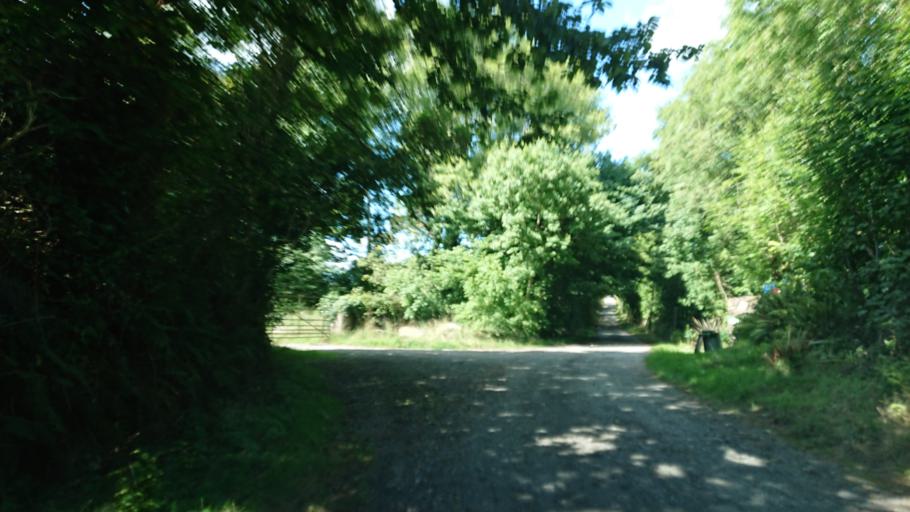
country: IE
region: Munster
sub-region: Waterford
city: Waterford
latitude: 52.2294
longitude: -7.1504
